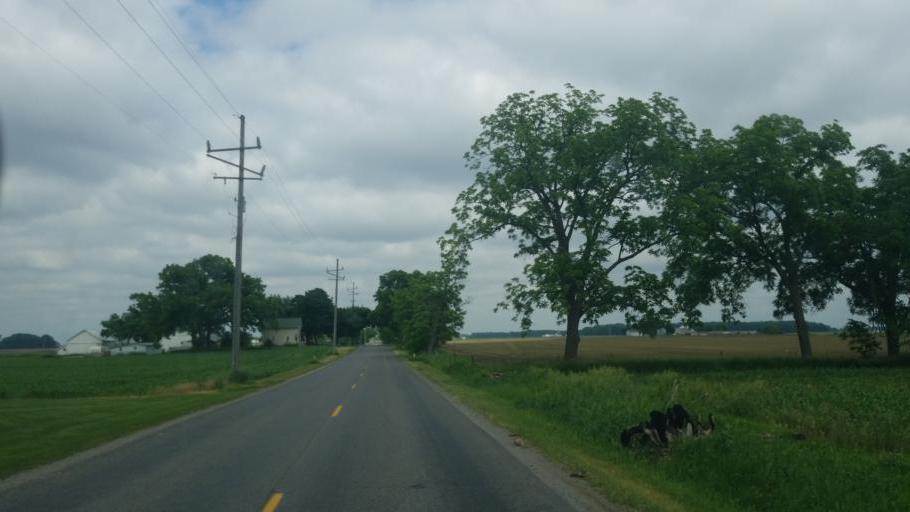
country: US
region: Indiana
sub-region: Elkhart County
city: Wakarusa
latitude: 41.4934
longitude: -86.0113
